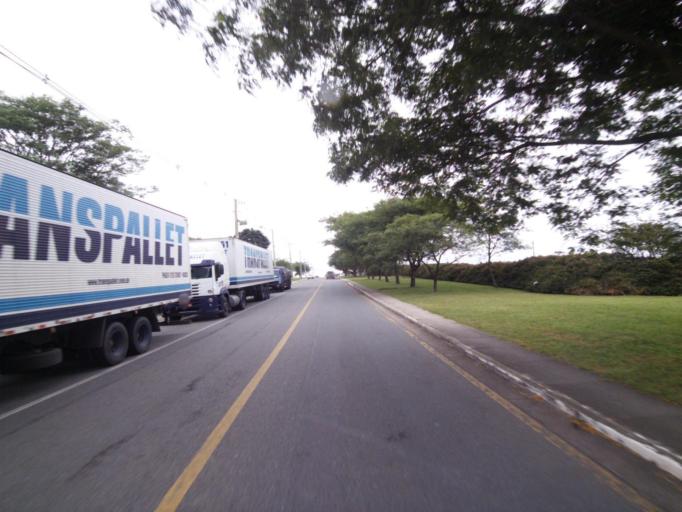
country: BR
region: Parana
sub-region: Sao Jose Dos Pinhais
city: Sao Jose dos Pinhais
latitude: -25.5339
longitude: -49.1786
